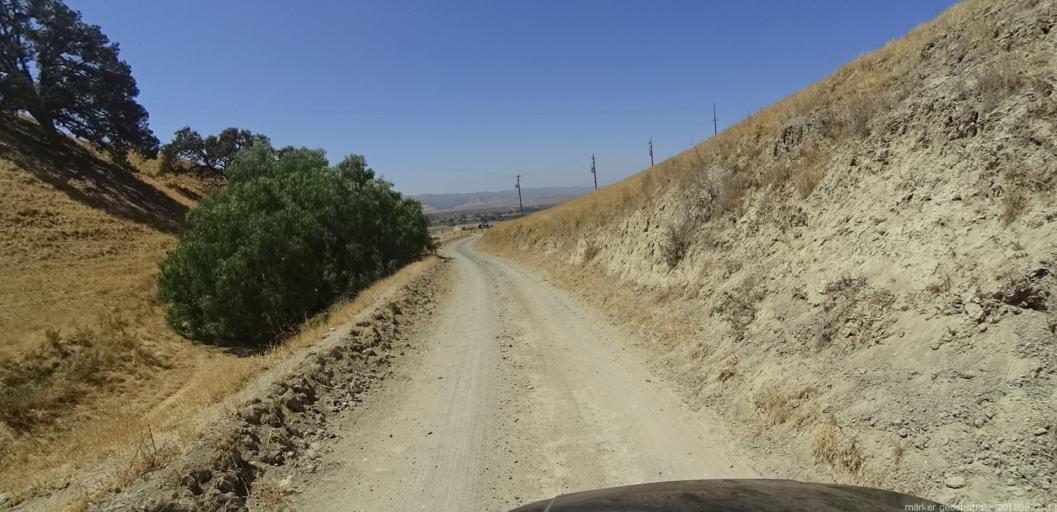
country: US
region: California
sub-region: Monterey County
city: King City
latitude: 36.0495
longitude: -120.9107
